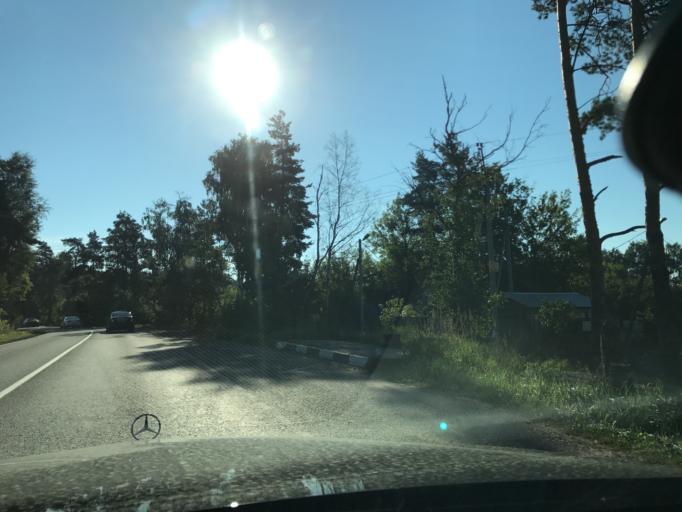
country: RU
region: Moskovskaya
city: Bakhchivandzhi
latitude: 55.8490
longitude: 38.1106
